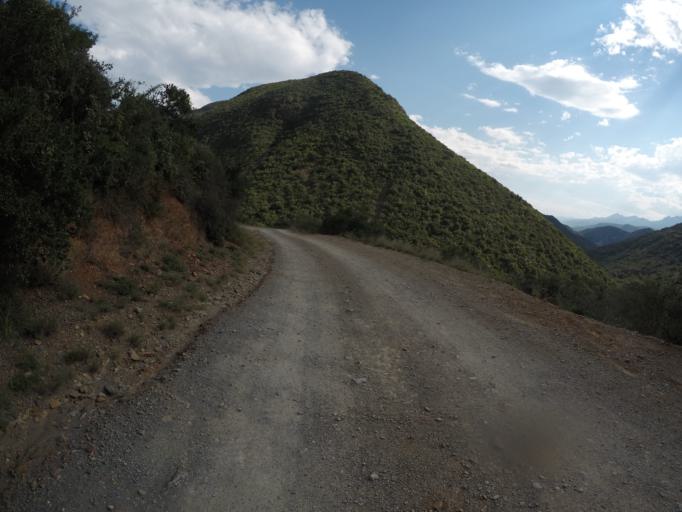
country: ZA
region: Eastern Cape
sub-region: Cacadu District Municipality
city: Kareedouw
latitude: -33.6490
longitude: 24.3372
